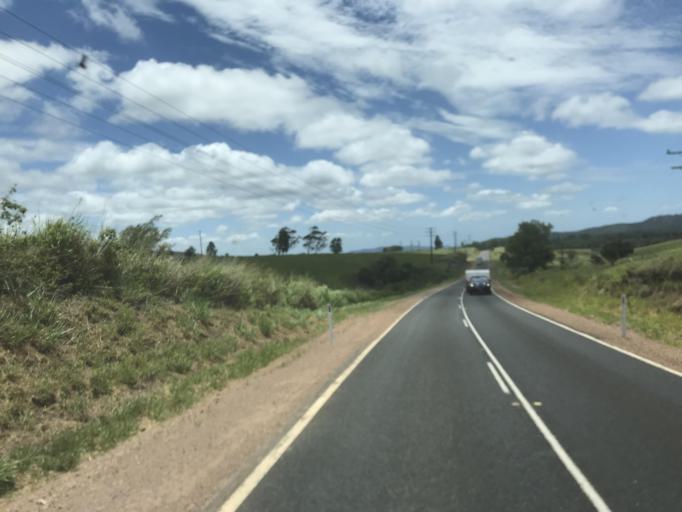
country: AU
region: Queensland
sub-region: Tablelands
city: Ravenshoe
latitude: -17.6031
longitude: 145.5140
